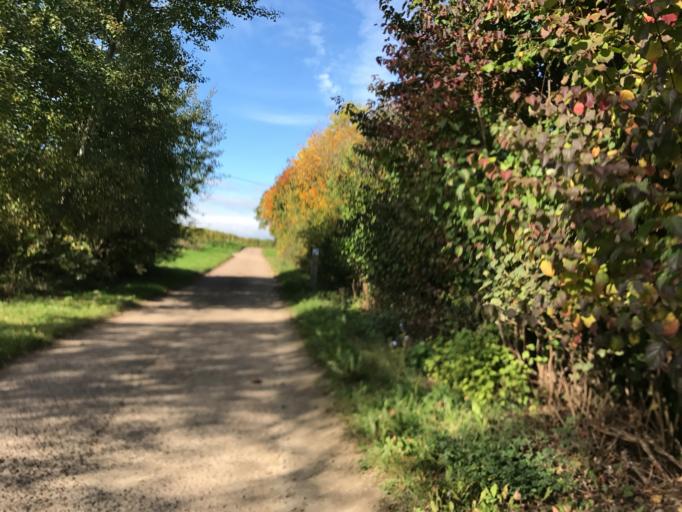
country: DE
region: Rheinland-Pfalz
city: Gau-Algesheim
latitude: 49.9462
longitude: 8.0158
